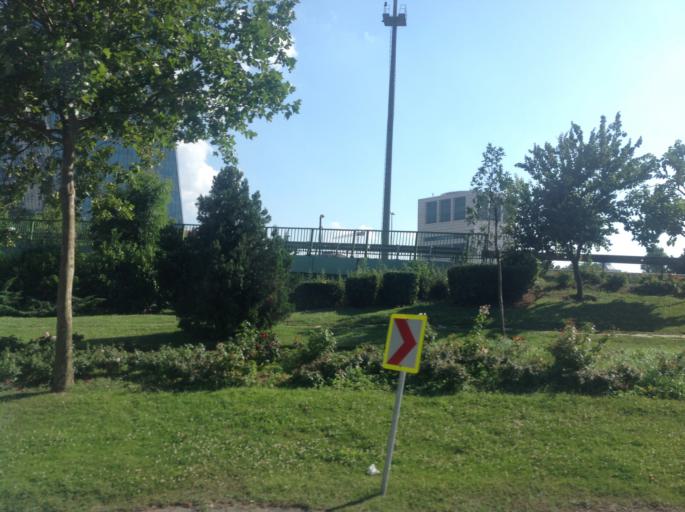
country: TR
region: Istanbul
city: Sisli
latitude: 41.0845
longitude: 29.0092
